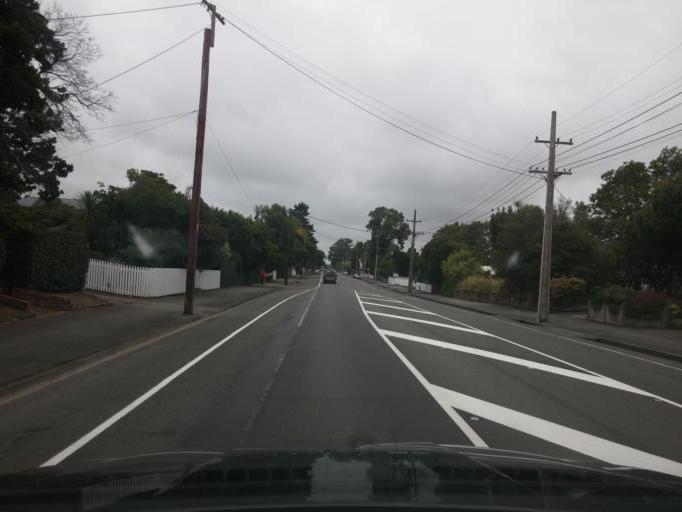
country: NZ
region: Wellington
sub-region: Masterton District
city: Masterton
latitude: -41.0865
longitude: 175.4535
